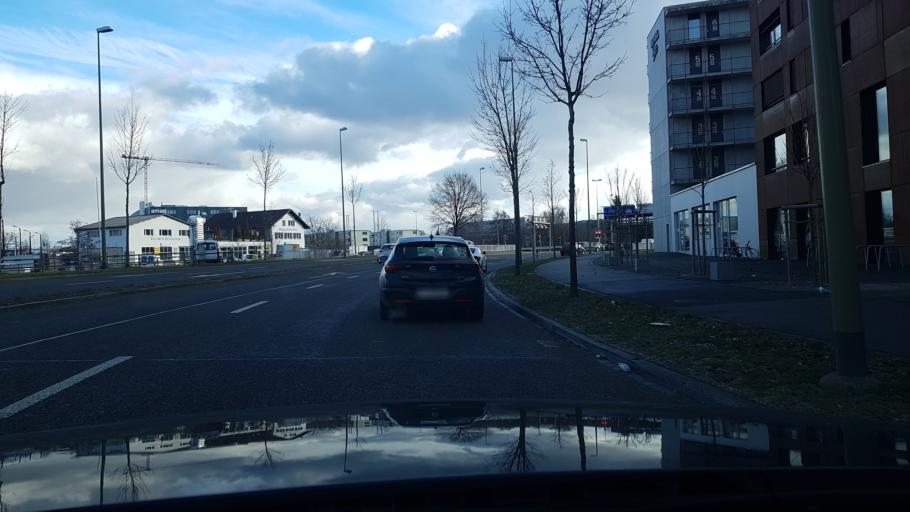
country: CH
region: Zurich
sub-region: Bezirk Uster
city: Duebendorf / Wasserfurren
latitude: 47.4040
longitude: 8.6055
